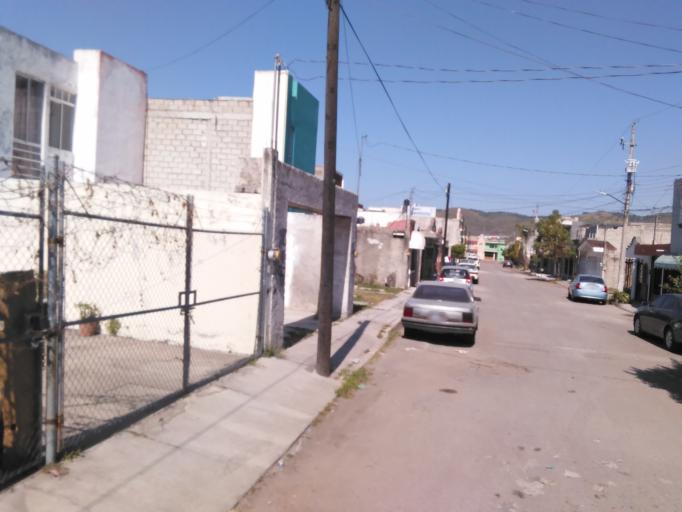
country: MX
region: Nayarit
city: Tepic
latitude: 21.4827
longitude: -104.8557
